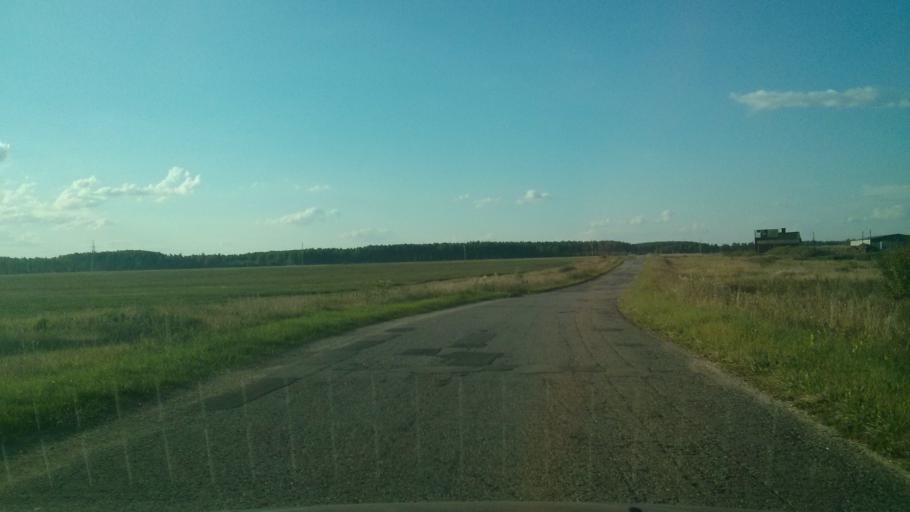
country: RU
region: Vladimir
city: Melenki
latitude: 55.3131
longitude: 41.7814
